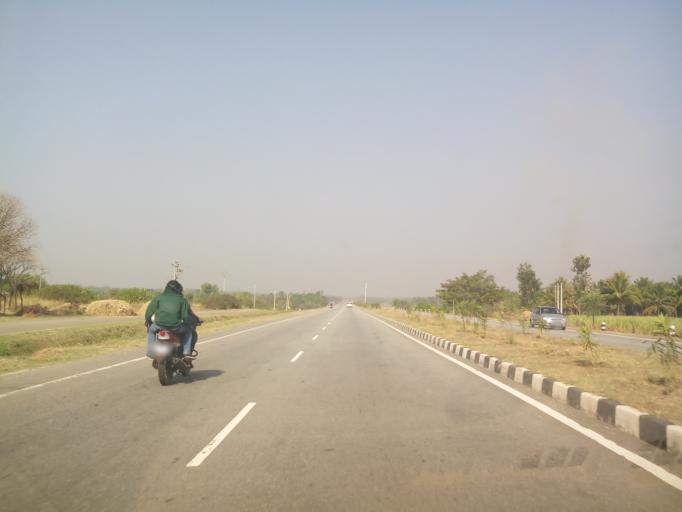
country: IN
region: Karnataka
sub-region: Tumkur
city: Kunigal
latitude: 13.0050
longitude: 77.0102
